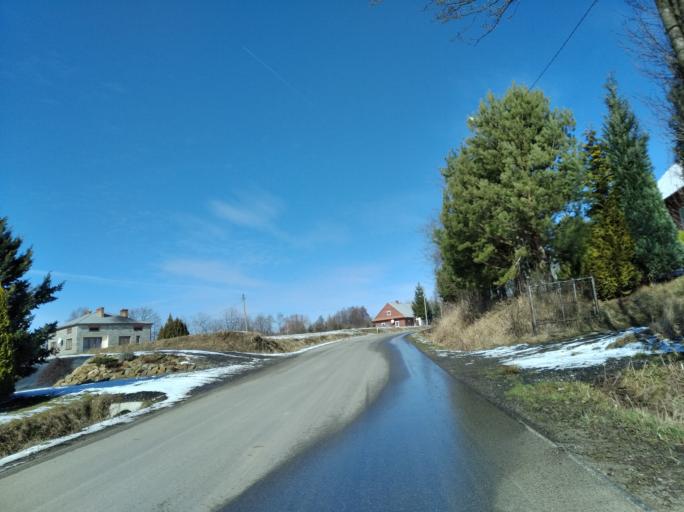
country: PL
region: Subcarpathian Voivodeship
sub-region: Powiat brzozowski
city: Jablonica Polska
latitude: 49.7207
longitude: 21.8800
